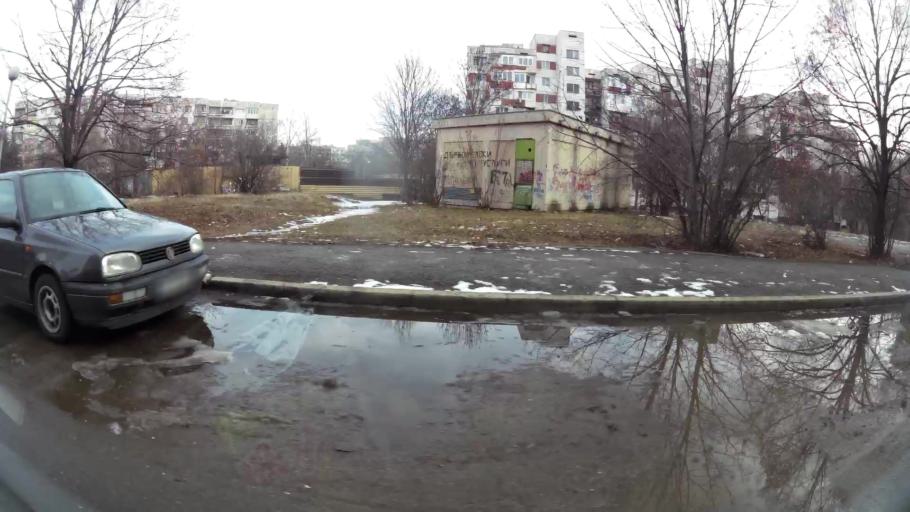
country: BG
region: Sofiya
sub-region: Obshtina Bozhurishte
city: Bozhurishte
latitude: 42.7170
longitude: 23.2407
